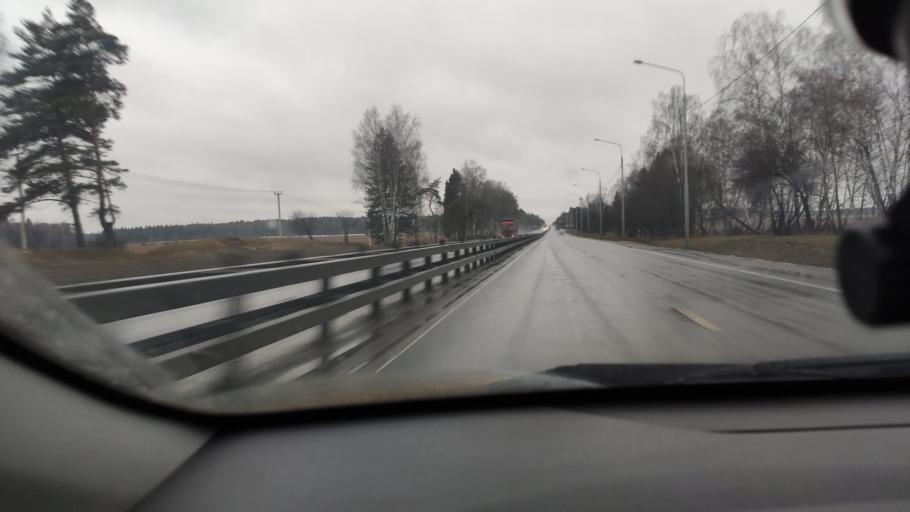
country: RU
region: Moskovskaya
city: Troitsk
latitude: 55.3384
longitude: 37.3029
